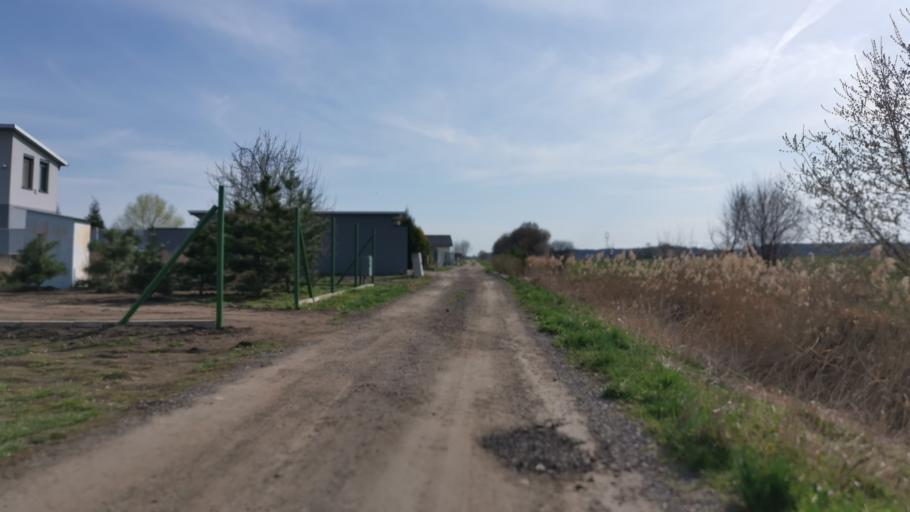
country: CZ
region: South Moravian
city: Tvrdonice
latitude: 48.7275
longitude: 17.0227
